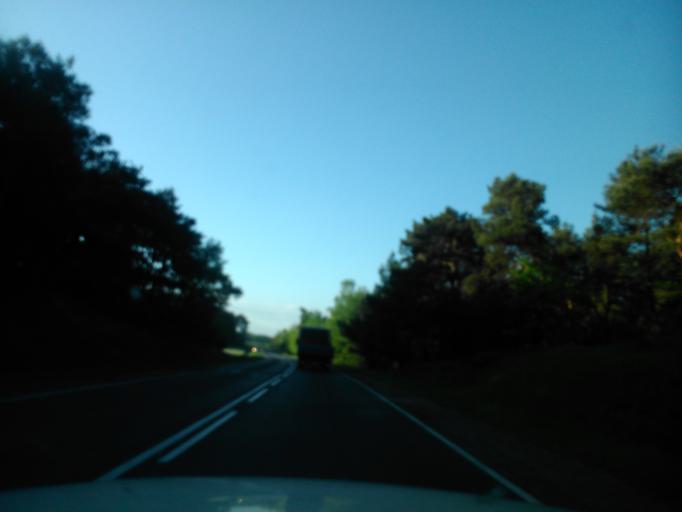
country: PL
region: Masovian Voivodeship
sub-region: Powiat plocki
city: Wyszogrod
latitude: 52.3480
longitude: 20.2101
